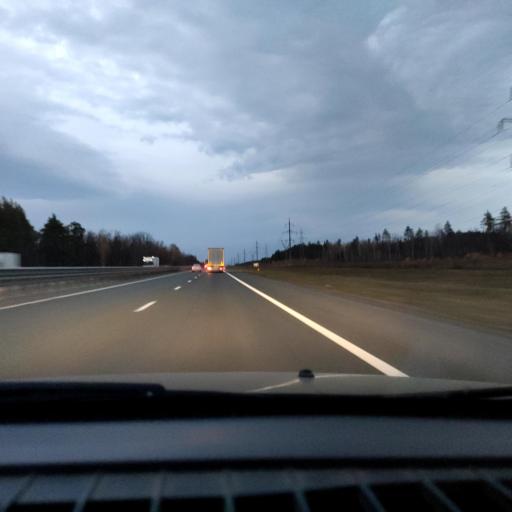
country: RU
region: Samara
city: Povolzhskiy
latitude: 53.5158
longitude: 49.6992
